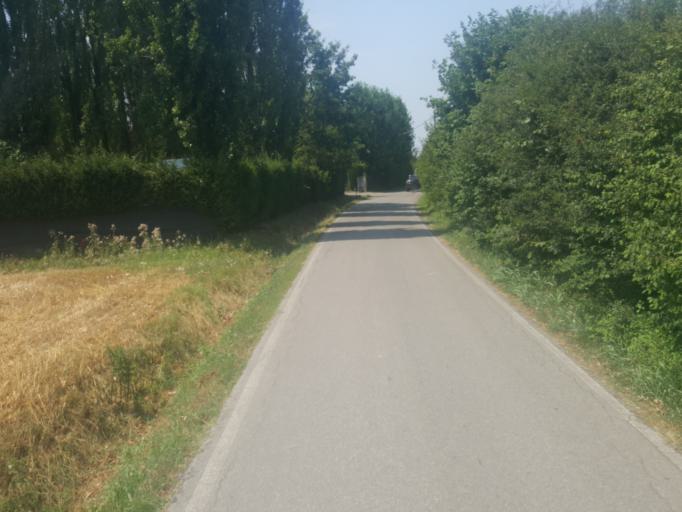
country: IT
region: Emilia-Romagna
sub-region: Provincia di Modena
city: Gaggio
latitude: 44.6367
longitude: 11.0076
